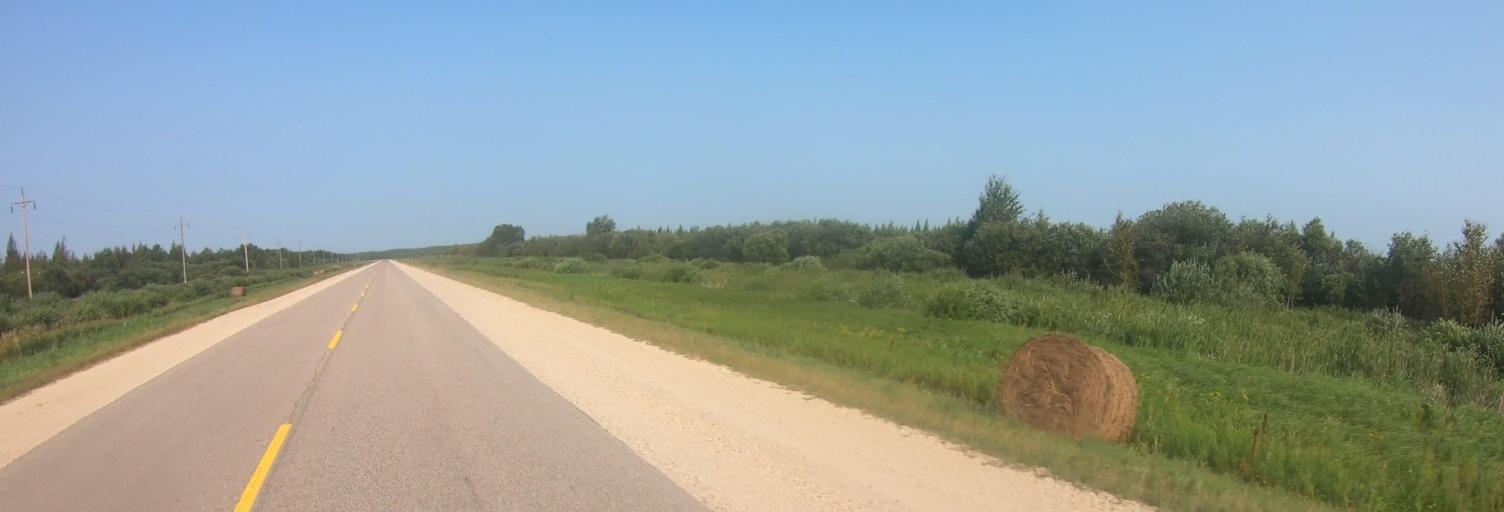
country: US
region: Minnesota
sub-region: Roseau County
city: Warroad
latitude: 49.0193
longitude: -95.5487
